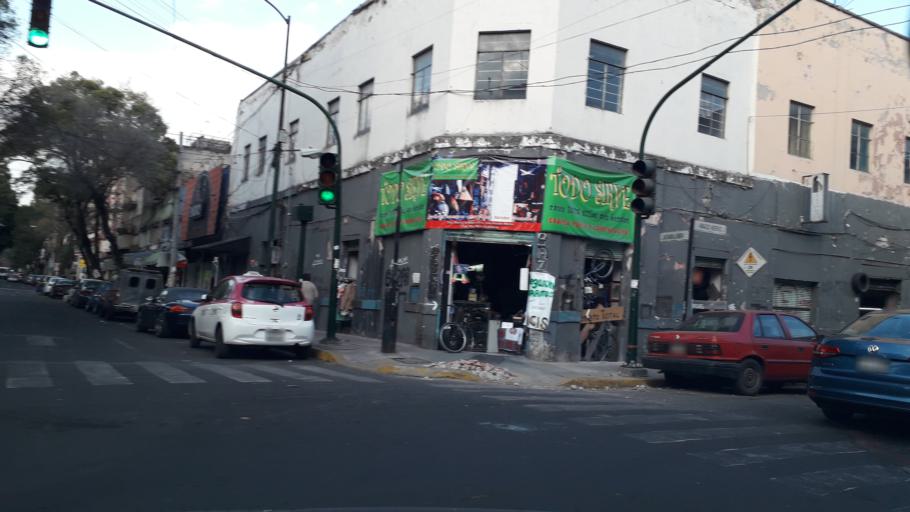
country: MX
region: Mexico City
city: Cuauhtemoc
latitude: 19.4432
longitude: -99.1580
